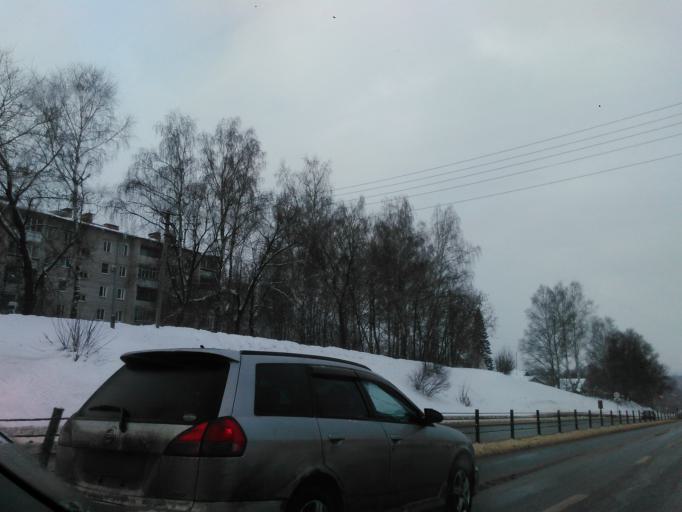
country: RU
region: Moskovskaya
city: Dedenevo
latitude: 56.2469
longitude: 37.5210
